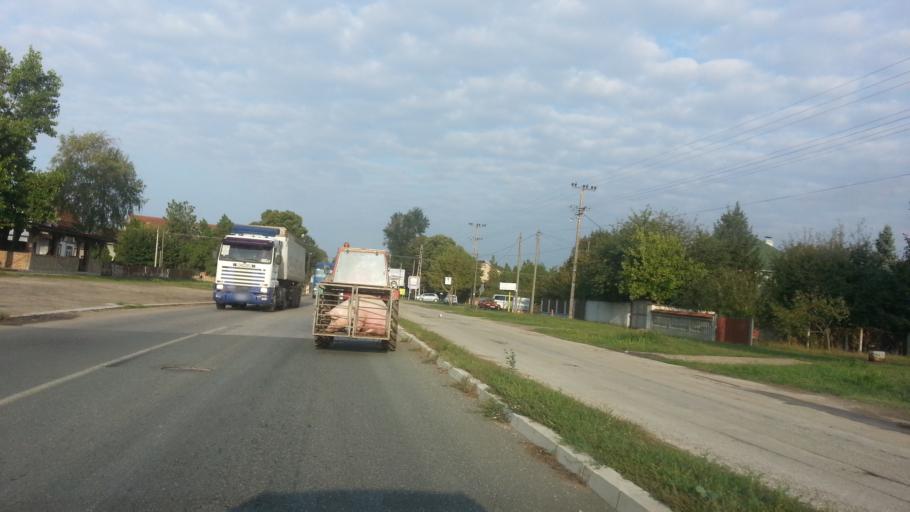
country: RS
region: Autonomna Pokrajina Vojvodina
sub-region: Sremski Okrug
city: Stara Pazova
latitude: 44.9868
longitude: 20.1843
